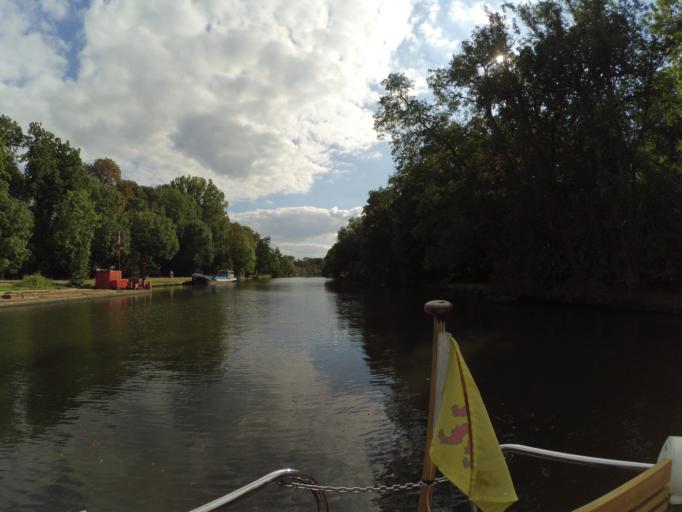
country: NL
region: Utrecht
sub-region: Stichtse Vecht
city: Breukelen
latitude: 52.1900
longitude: 5.0060
